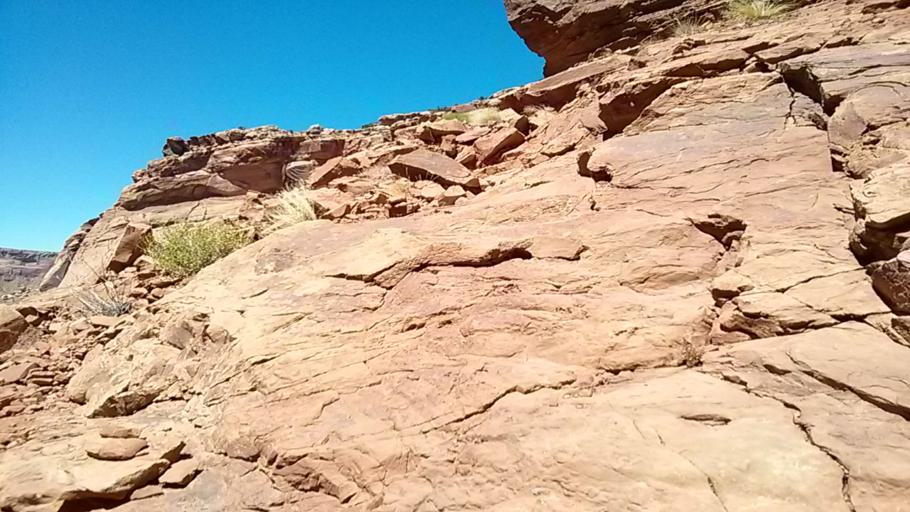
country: US
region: Utah
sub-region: Grand County
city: Moab
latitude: 38.4529
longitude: -109.9450
